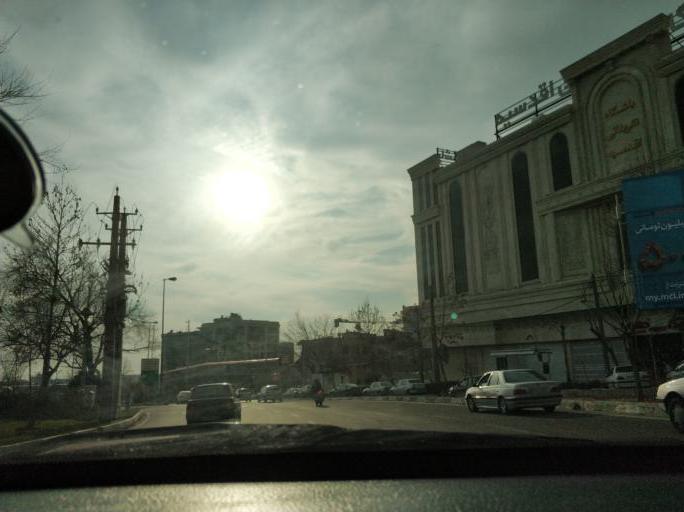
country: IR
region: Tehran
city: Tajrish
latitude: 35.8020
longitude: 51.4866
